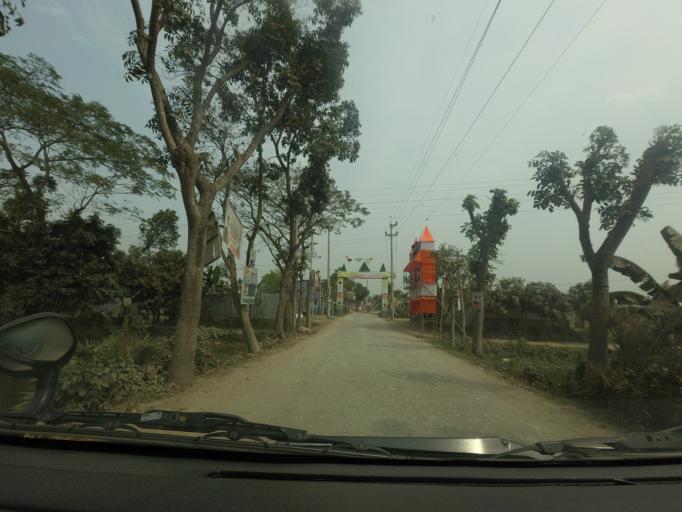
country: BD
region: Dhaka
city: Kishorganj
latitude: 24.3447
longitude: 90.7665
